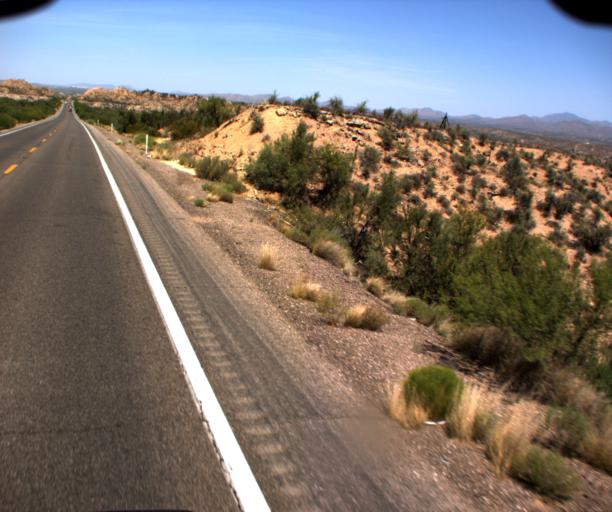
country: US
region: Arizona
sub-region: Gila County
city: San Carlos
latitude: 33.3433
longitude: -110.6097
